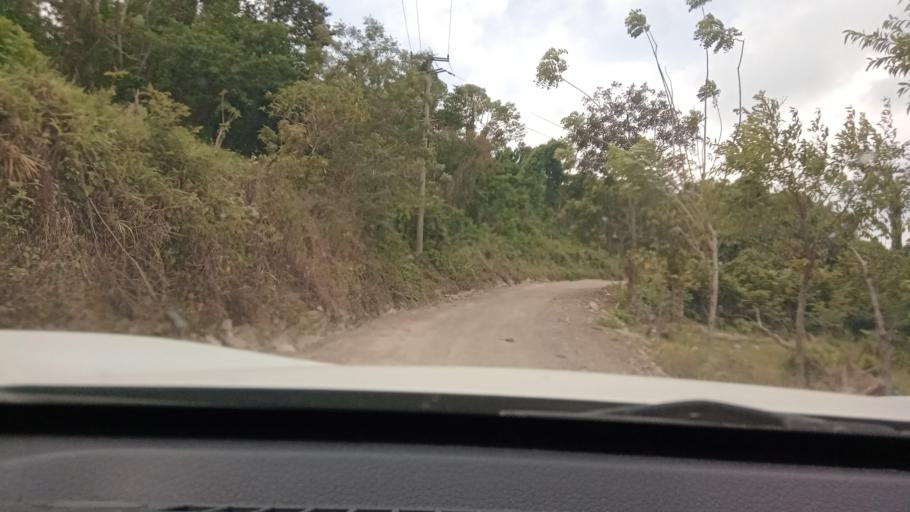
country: MX
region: Tabasco
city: Chontalpa
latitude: 17.4996
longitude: -93.6465
